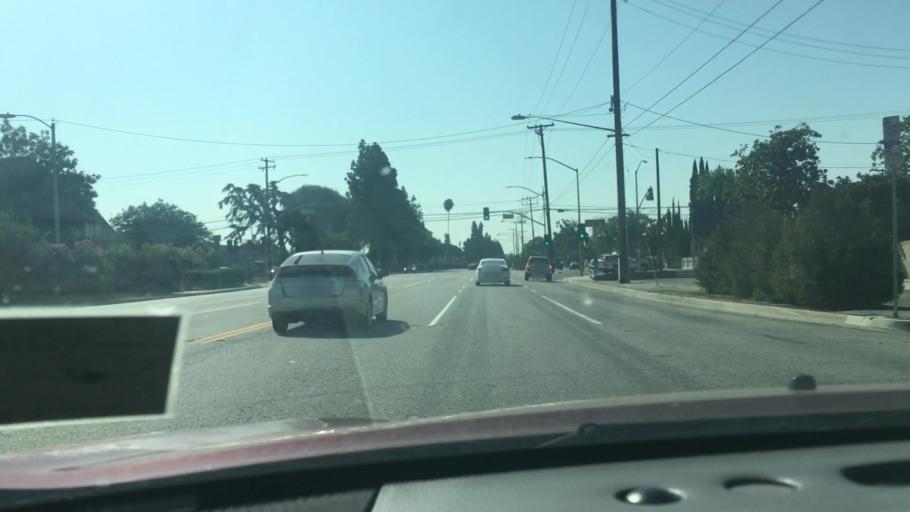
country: US
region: California
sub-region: Los Angeles County
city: South Whittier
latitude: 33.9461
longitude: -118.0321
